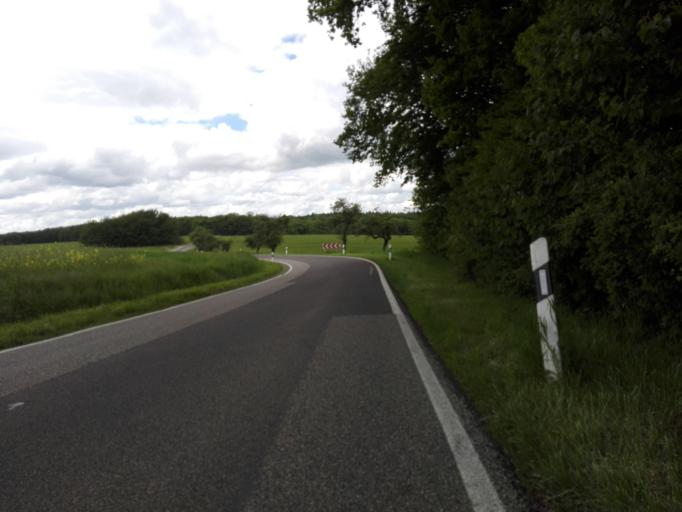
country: DE
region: Baden-Wuerttemberg
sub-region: Regierungsbezirk Stuttgart
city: Kuenzelsau
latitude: 49.3171
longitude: 9.7134
